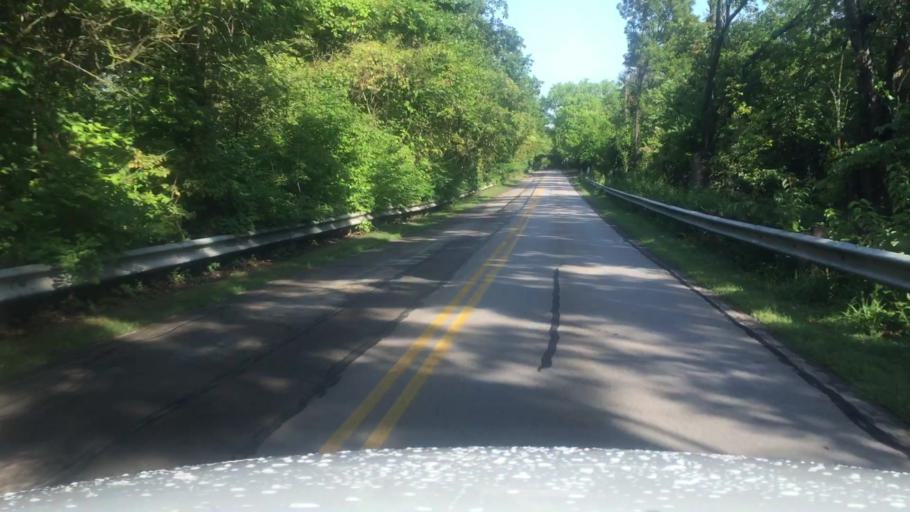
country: US
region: Kansas
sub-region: Johnson County
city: Shawnee
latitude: 39.0483
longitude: -94.7631
